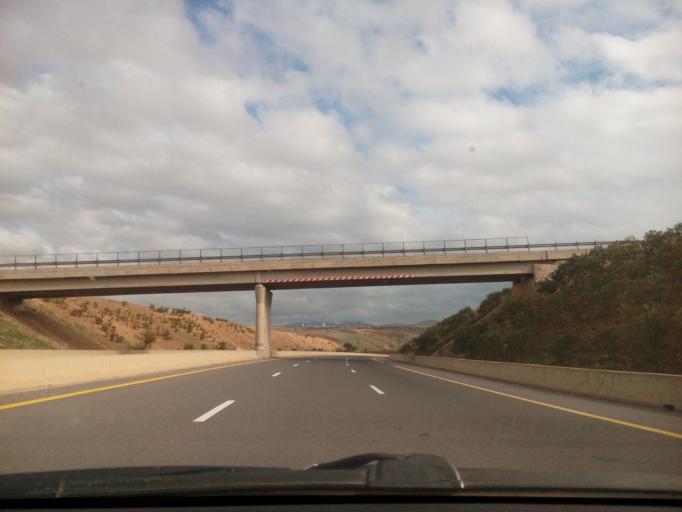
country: DZ
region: Tlemcen
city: Chetouane
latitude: 34.9603
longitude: -1.2921
